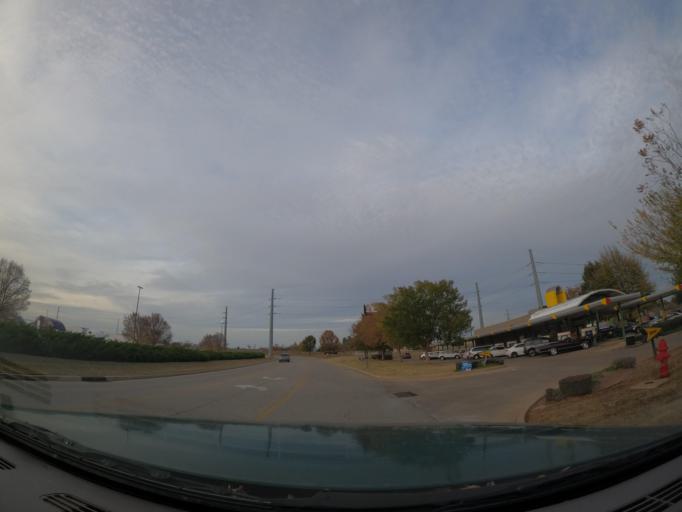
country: US
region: Oklahoma
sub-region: Tulsa County
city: Broken Arrow
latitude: 35.9915
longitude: -95.7982
